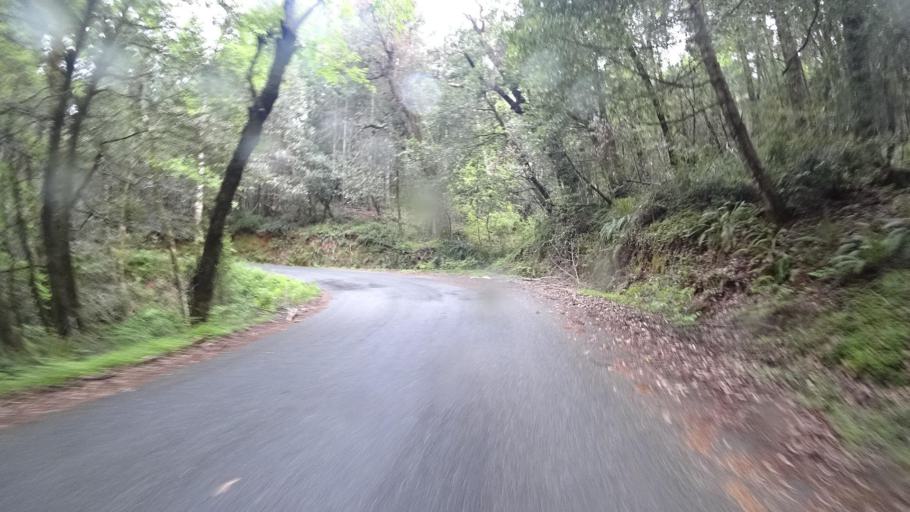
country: US
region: California
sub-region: Humboldt County
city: Willow Creek
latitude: 41.2035
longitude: -123.7764
